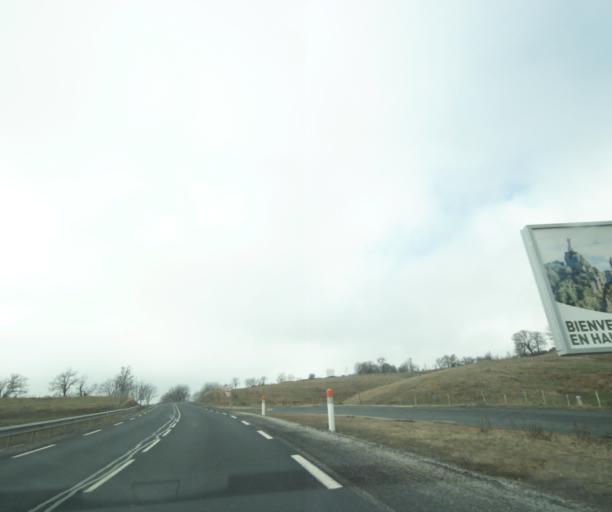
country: FR
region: Languedoc-Roussillon
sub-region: Departement de la Lozere
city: Langogne
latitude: 44.7606
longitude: 3.8885
